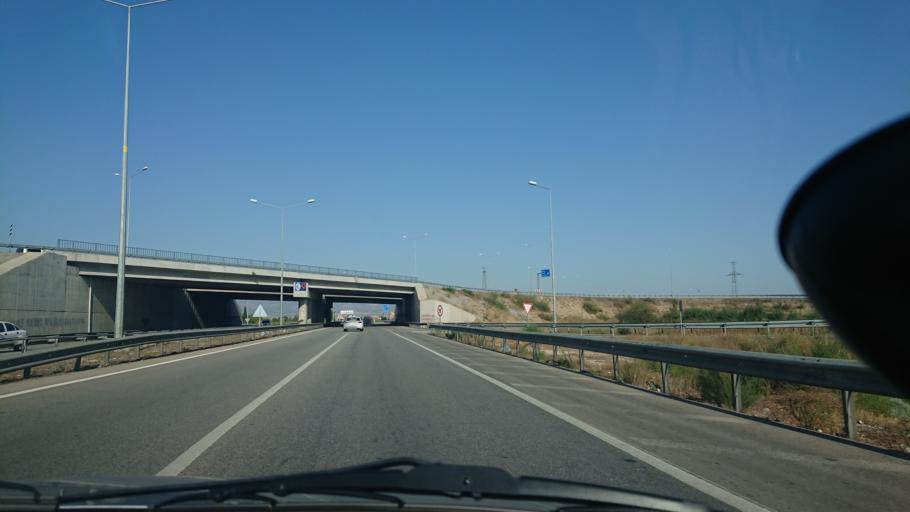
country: TR
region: Manisa
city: Salihli
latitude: 38.4994
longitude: 28.2012
